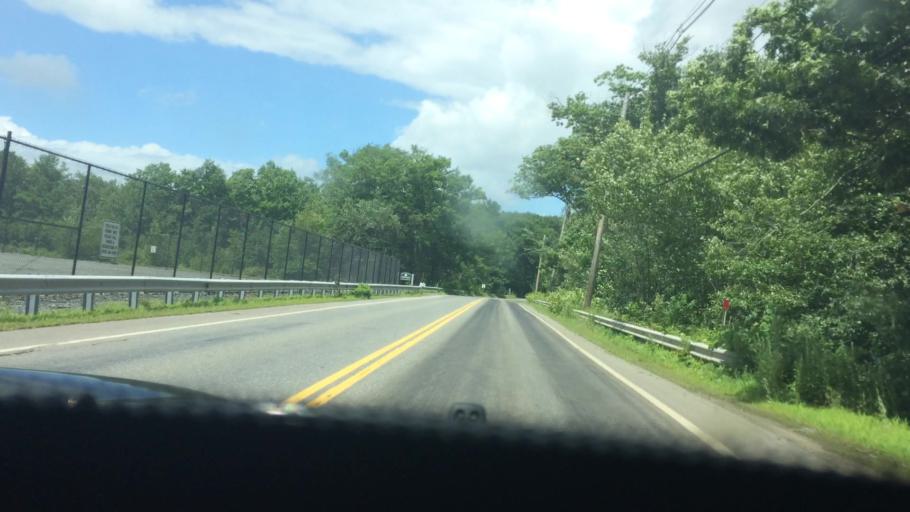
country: US
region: Massachusetts
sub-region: Middlesex County
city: Maynard
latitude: 42.4063
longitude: -71.4395
